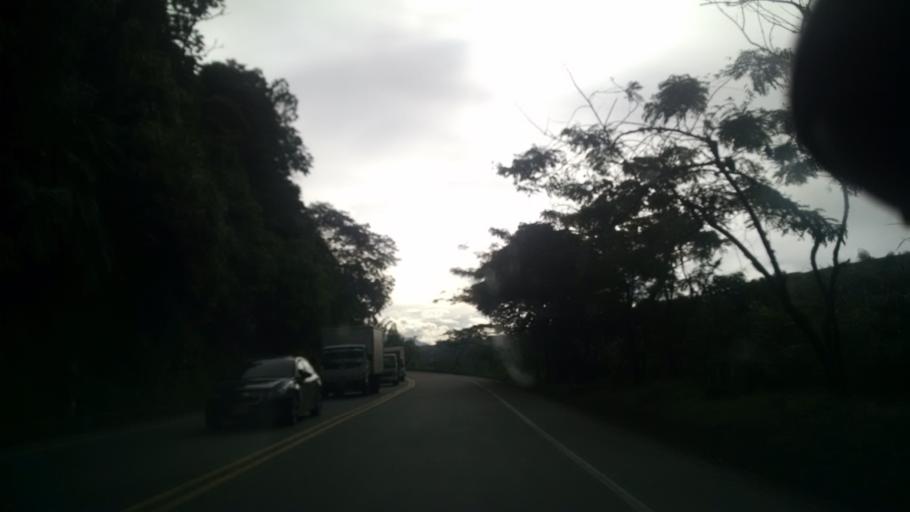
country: CO
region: Risaralda
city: Pereira
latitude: 4.8191
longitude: -75.7337
